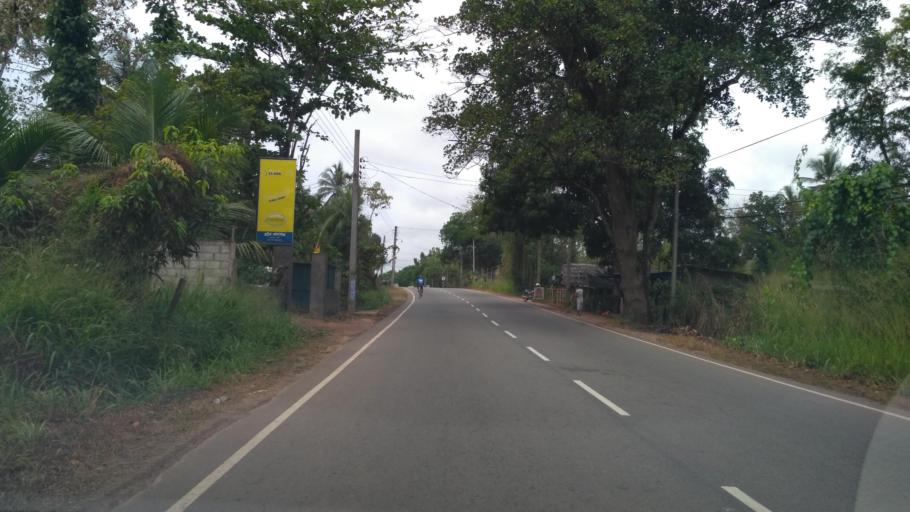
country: LK
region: North Western
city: Kuliyapitiya
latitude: 7.3265
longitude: 80.0458
